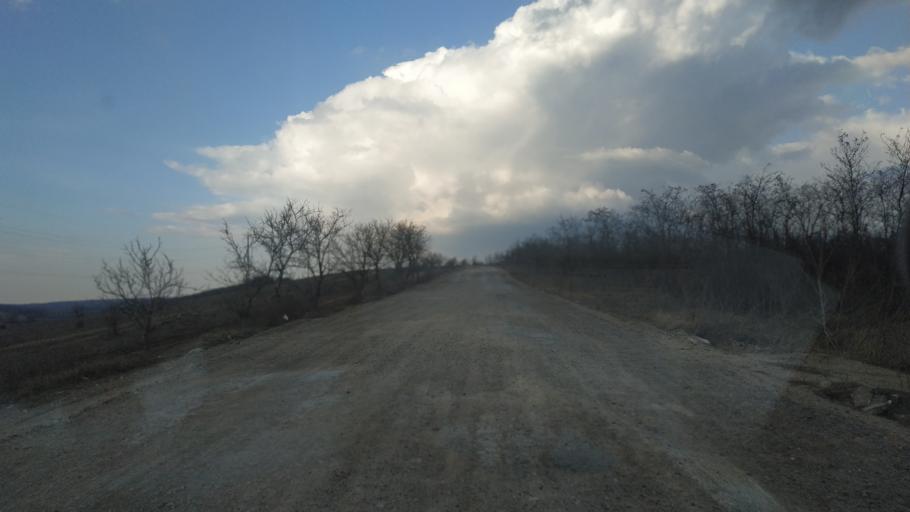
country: MD
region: Anenii Noi
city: Anenii Noi
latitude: 46.9881
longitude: 29.2844
